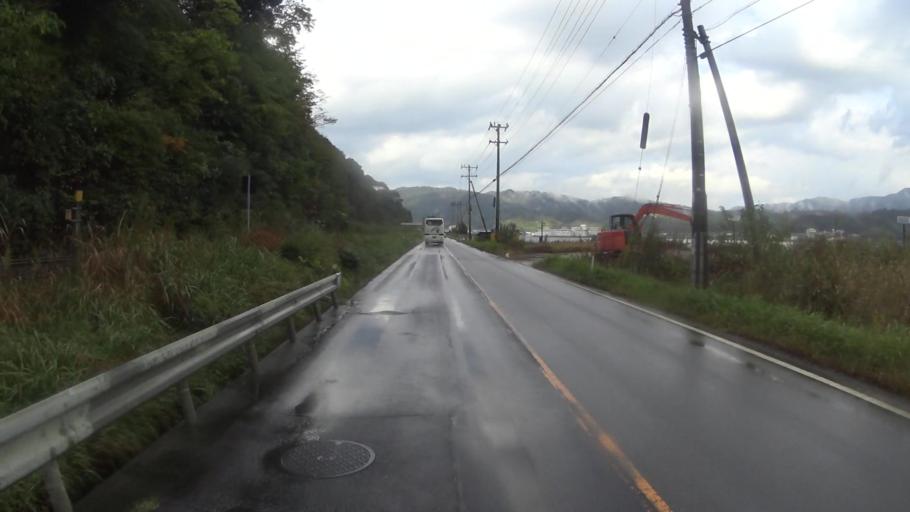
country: JP
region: Kyoto
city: Miyazu
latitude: 35.5611
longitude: 135.1735
